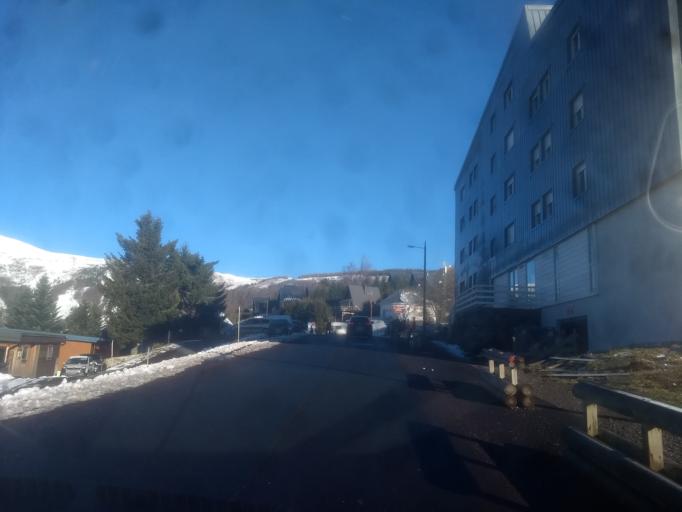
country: FR
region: Auvergne
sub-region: Departement du Puy-de-Dome
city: Mont-Dore
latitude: 45.5068
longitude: 2.8613
